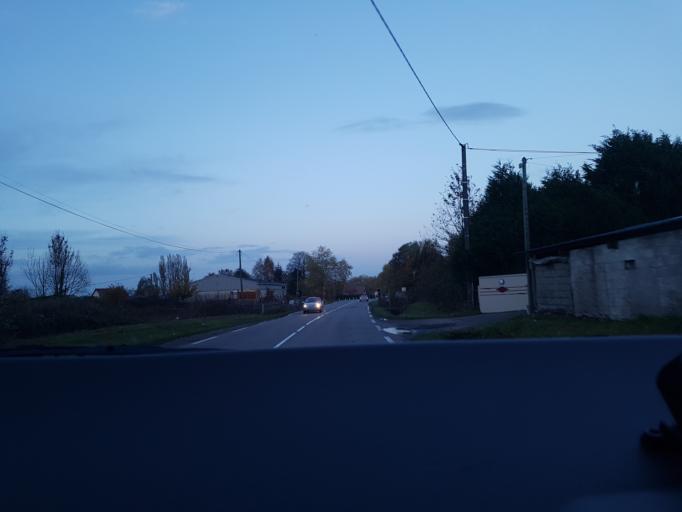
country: FR
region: Haute-Normandie
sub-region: Departement de l'Eure
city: Beuzeville
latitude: 49.3427
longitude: 0.3593
